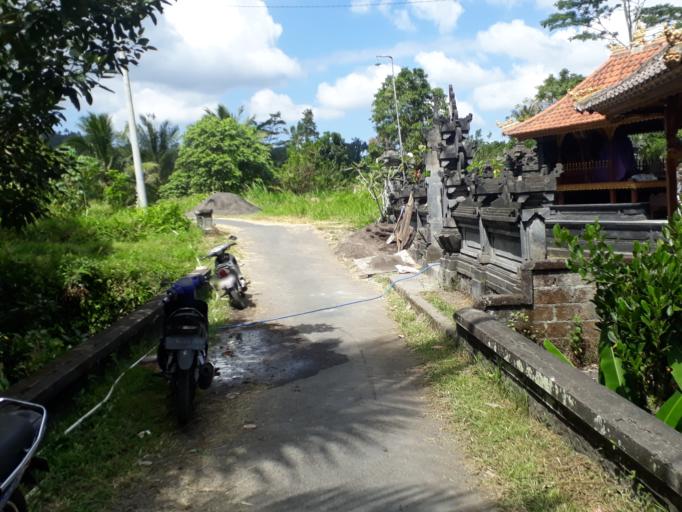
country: ID
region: Bali
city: Banjar Wangsian
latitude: -8.4593
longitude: 115.4446
